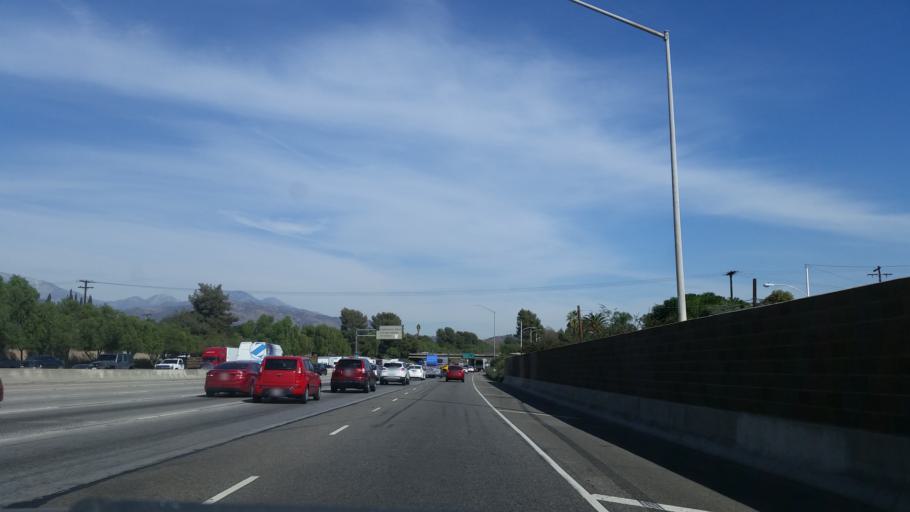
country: US
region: California
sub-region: Los Angeles County
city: Citrus
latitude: 34.1207
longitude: -117.9038
